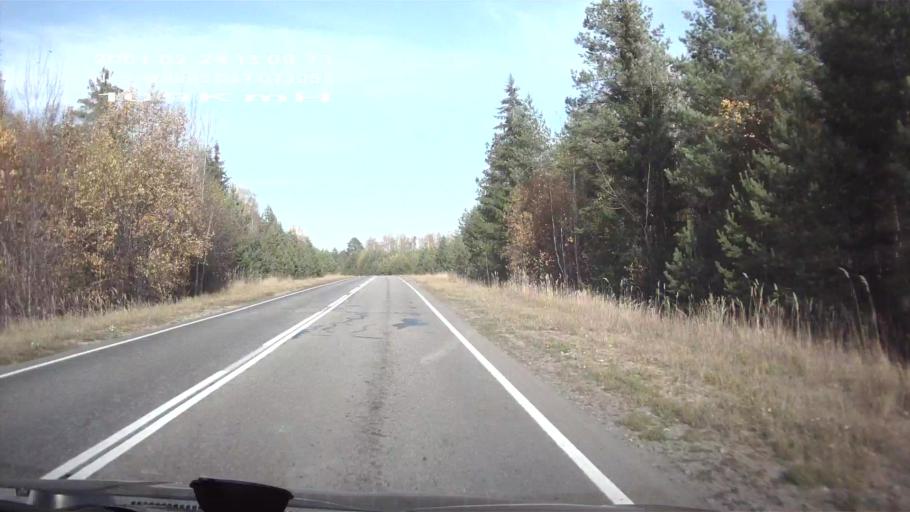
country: RU
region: Chuvashia
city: Buinsk
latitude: 55.1901
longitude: 47.0731
